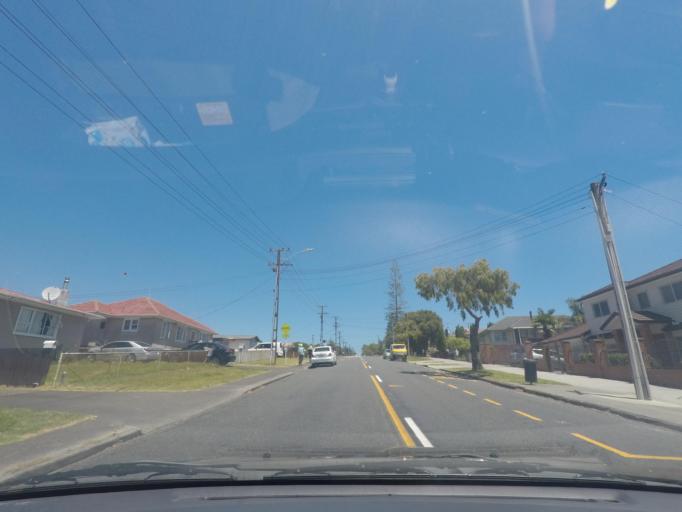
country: NZ
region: Auckland
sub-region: Auckland
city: Waitakere
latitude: -36.9145
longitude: 174.7160
